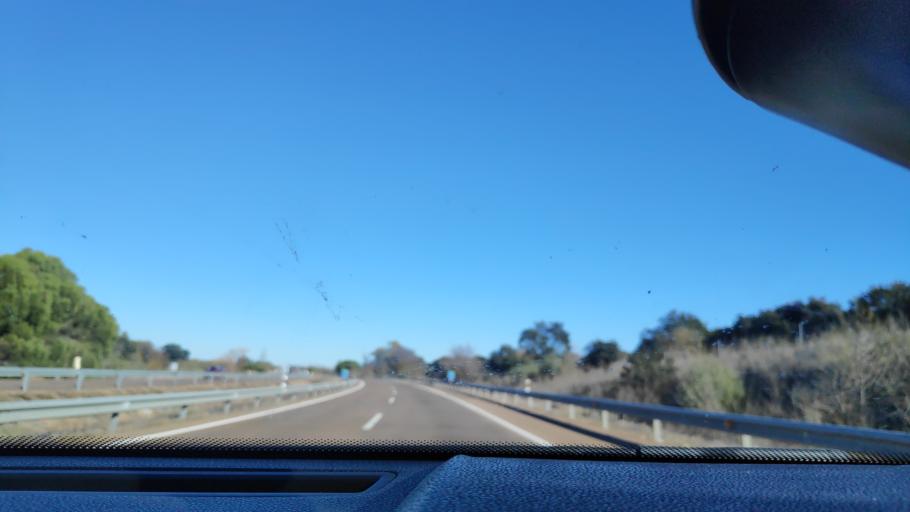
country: ES
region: Extremadura
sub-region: Provincia de Badajoz
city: Torremayor
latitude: 38.8601
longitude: -6.5338
